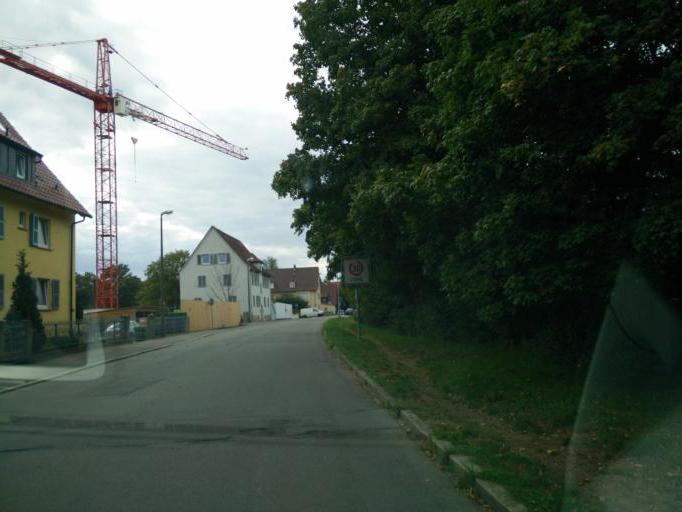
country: DE
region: Baden-Wuerttemberg
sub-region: Tuebingen Region
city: Tuebingen
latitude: 48.5172
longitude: 9.0704
